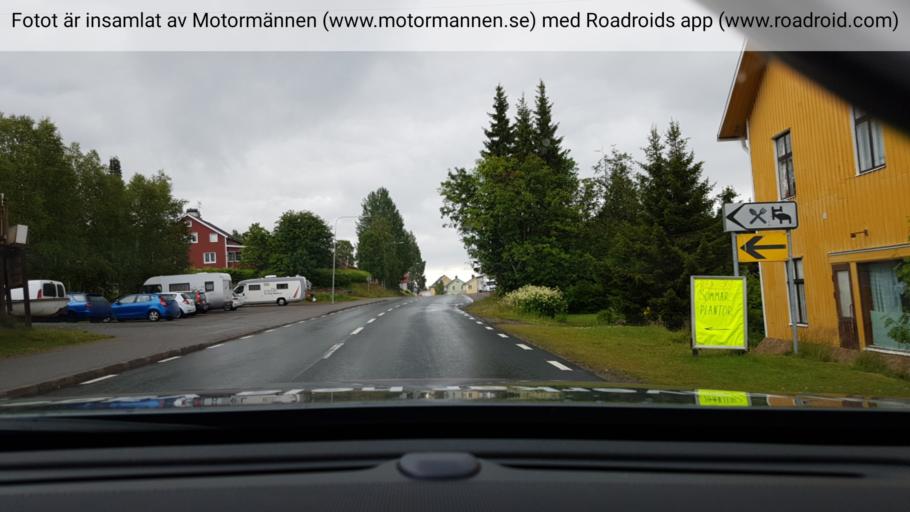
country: SE
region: Vaesterbotten
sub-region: Norsjo Kommun
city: Norsjoe
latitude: 65.2616
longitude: 19.6251
